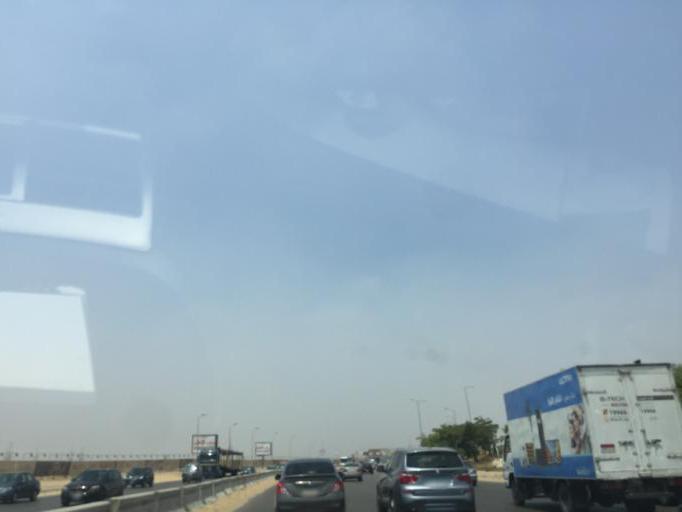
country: EG
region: Muhafazat al Qalyubiyah
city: Al Khankah
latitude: 30.0789
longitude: 31.4252
